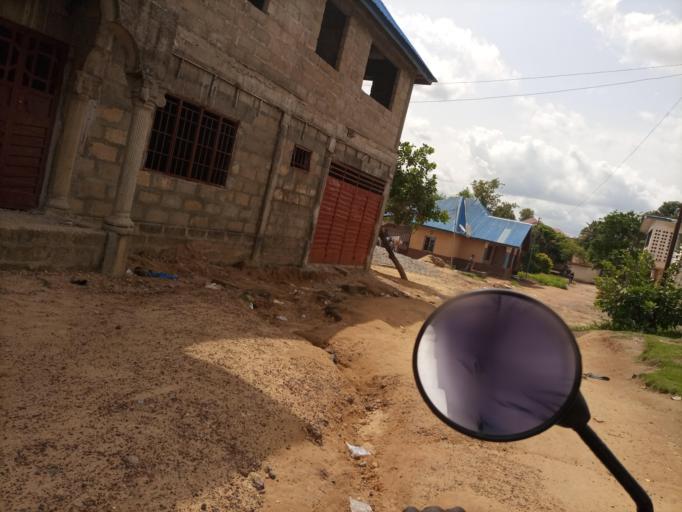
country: SL
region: Southern Province
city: Bo
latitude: 7.9480
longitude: -11.7368
